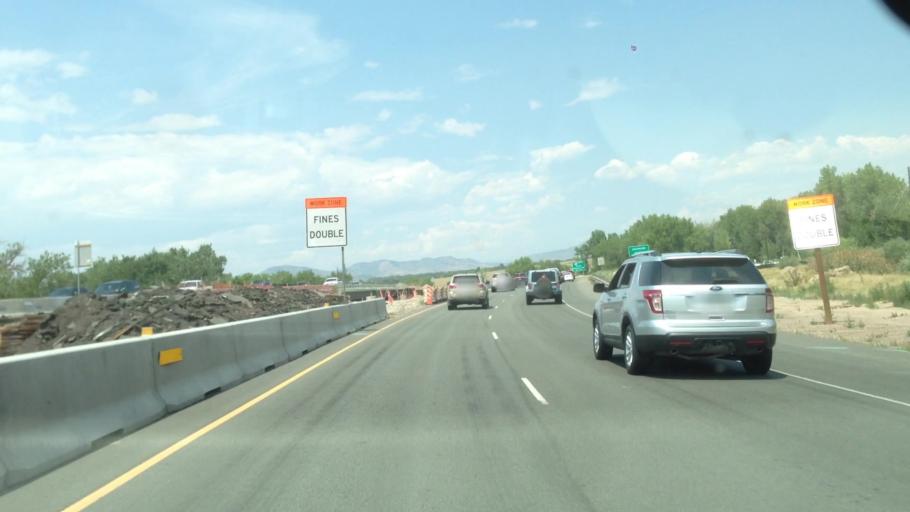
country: US
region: Colorado
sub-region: Arapahoe County
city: Columbine Valley
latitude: 39.5656
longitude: -105.0395
